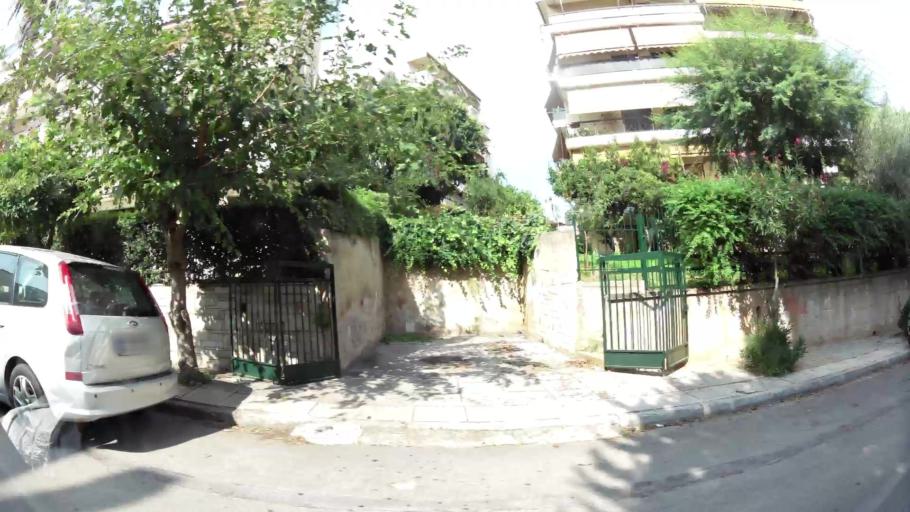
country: GR
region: Attica
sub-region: Nomarchia Athinas
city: Cholargos
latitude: 37.9920
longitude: 23.8036
